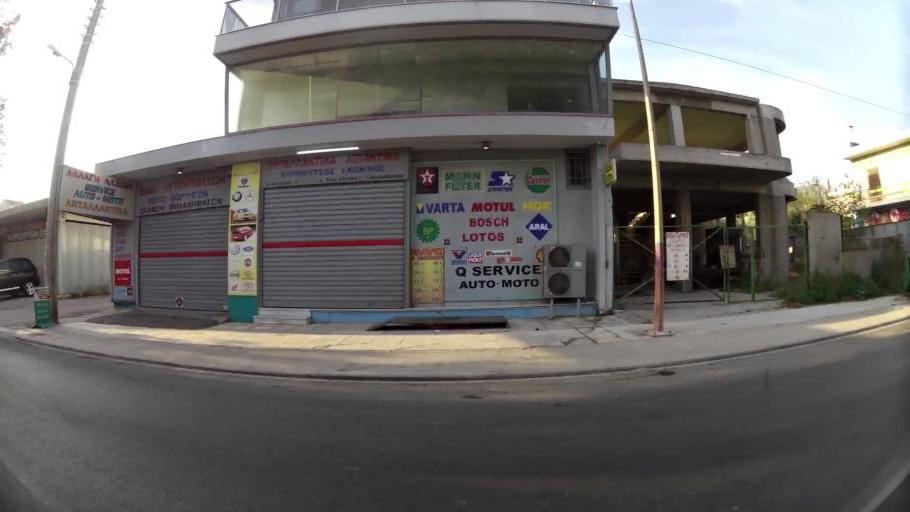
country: GR
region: Attica
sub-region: Nomarchia Dytikis Attikis
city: Zefyri
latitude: 38.0695
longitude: 23.7067
